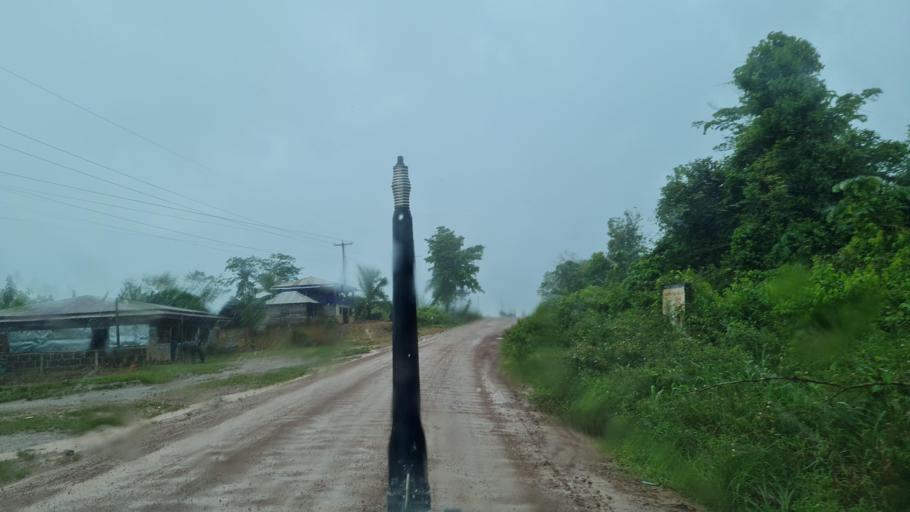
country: NI
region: Atlantico Norte (RAAN)
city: Puerto Cabezas
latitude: 14.0862
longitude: -83.8453
